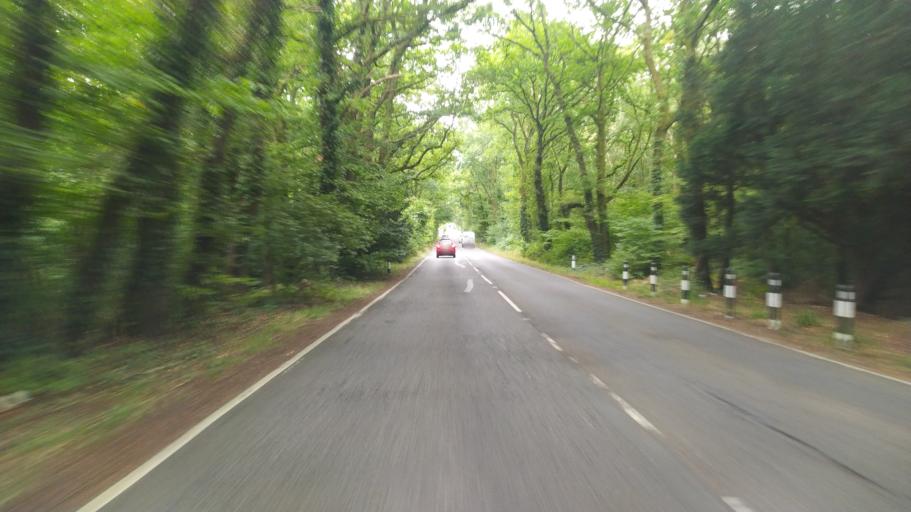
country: GB
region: England
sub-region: Hampshire
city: Havant
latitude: 50.8926
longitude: -0.9773
